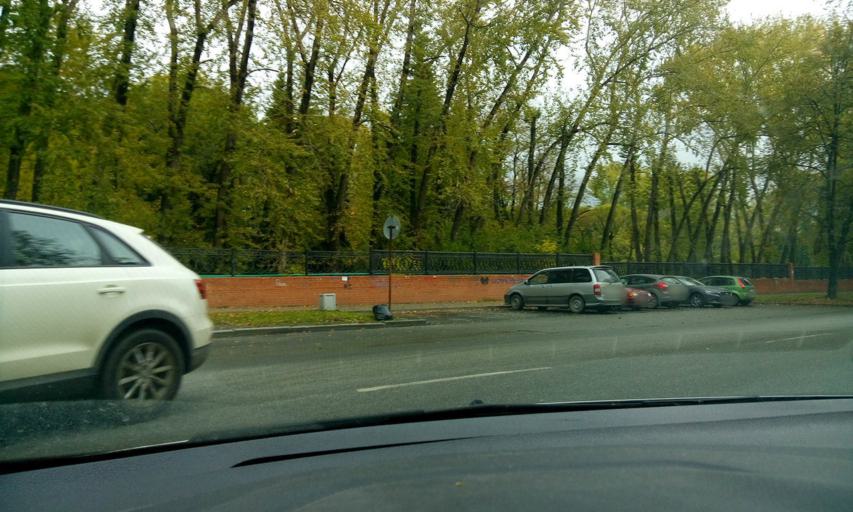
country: RU
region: Sverdlovsk
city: Yekaterinburg
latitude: 56.8485
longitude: 60.6484
